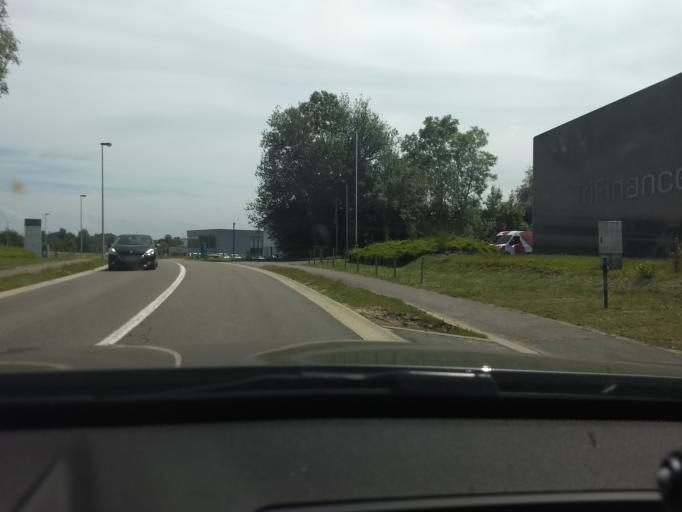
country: BE
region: Wallonia
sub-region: Province du Brabant Wallon
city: Louvain-la-Neuve
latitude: 50.6601
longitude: 4.6177
